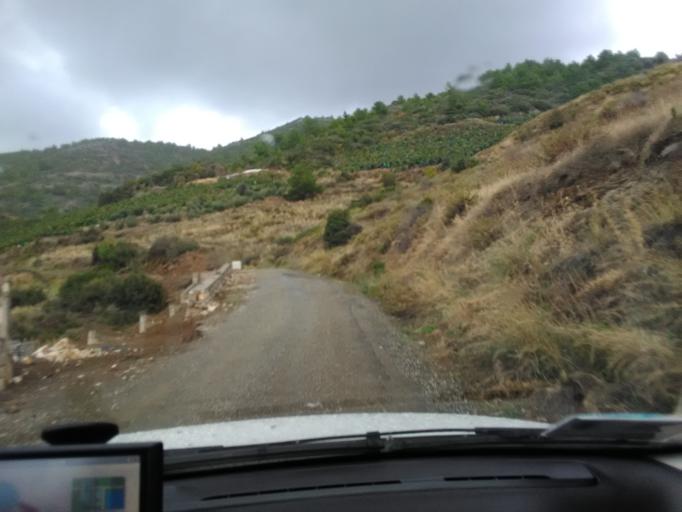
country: TR
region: Antalya
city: Gazipasa
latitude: 36.1603
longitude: 32.4213
